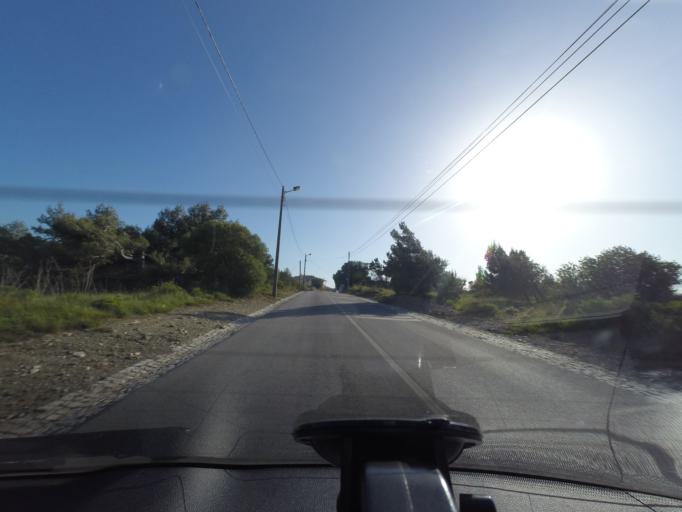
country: PT
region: Lisbon
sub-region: Cascais
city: Alcabideche
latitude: 38.7452
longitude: -9.4317
